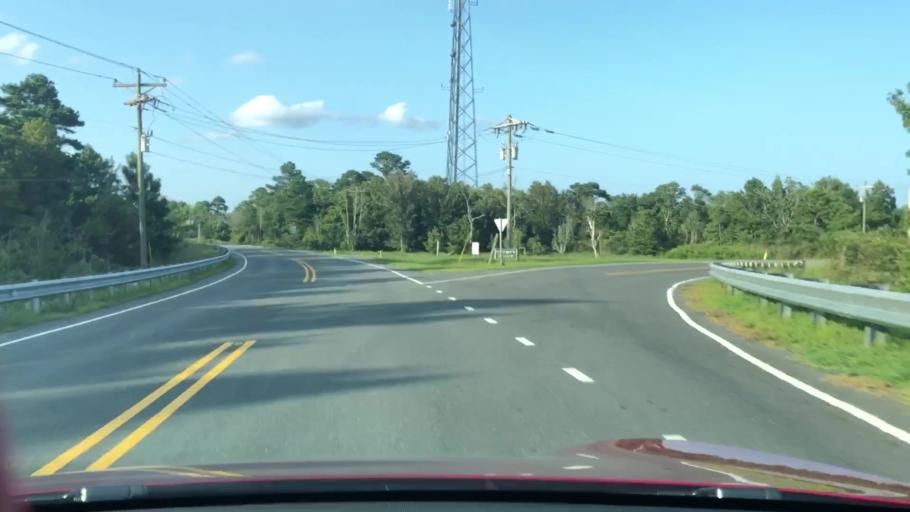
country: US
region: North Carolina
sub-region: Dare County
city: Wanchese
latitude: 35.7064
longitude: -75.7687
